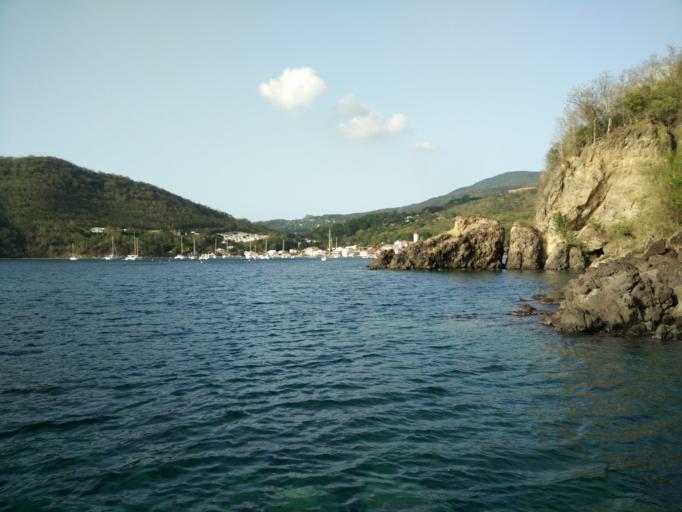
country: GP
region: Guadeloupe
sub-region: Guadeloupe
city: Pointe-Noire
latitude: 16.3039
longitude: -61.7993
